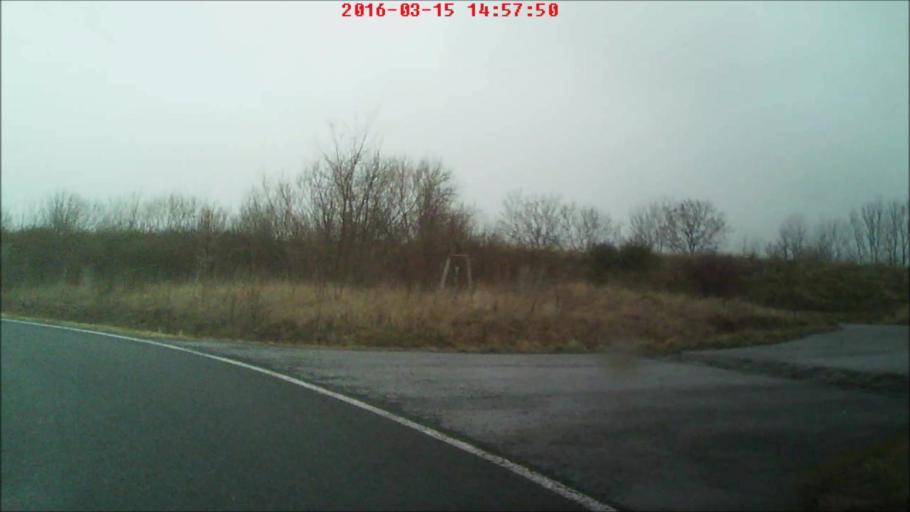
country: DE
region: Thuringia
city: Rockhausen
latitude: 50.9068
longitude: 11.0369
